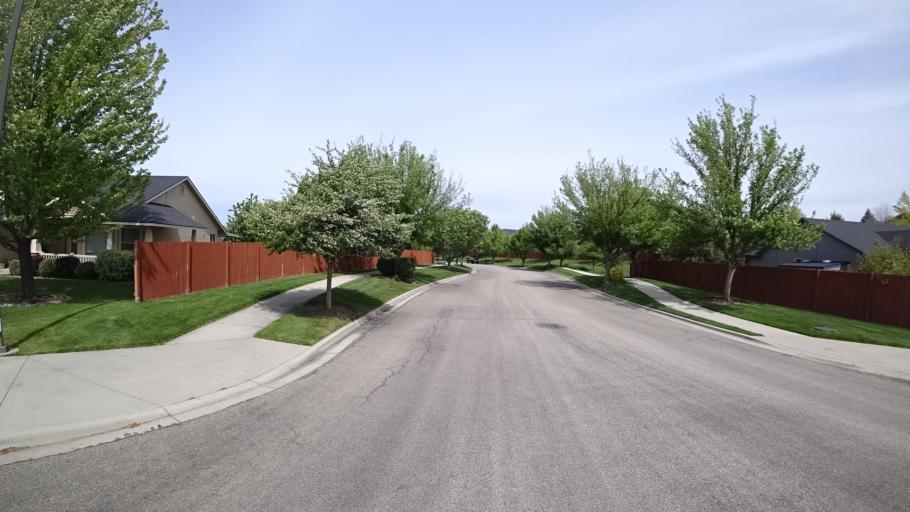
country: US
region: Idaho
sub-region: Ada County
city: Meridian
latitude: 43.5522
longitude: -116.3360
